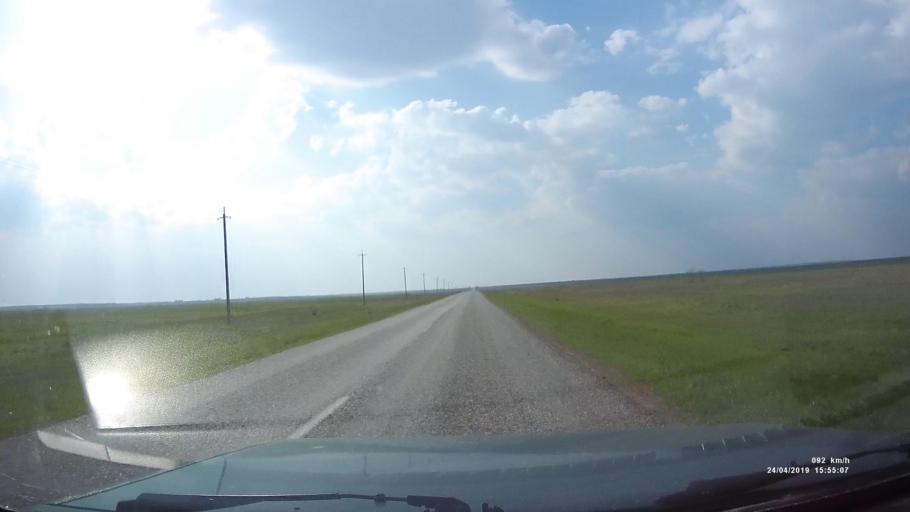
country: RU
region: Kalmykiya
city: Yashalta
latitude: 46.5882
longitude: 42.5556
